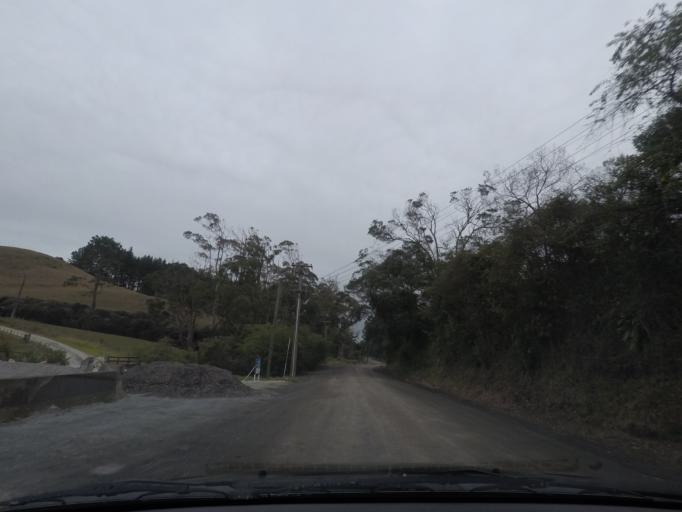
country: NZ
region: Auckland
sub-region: Auckland
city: Muriwai Beach
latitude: -36.7528
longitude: 174.5753
